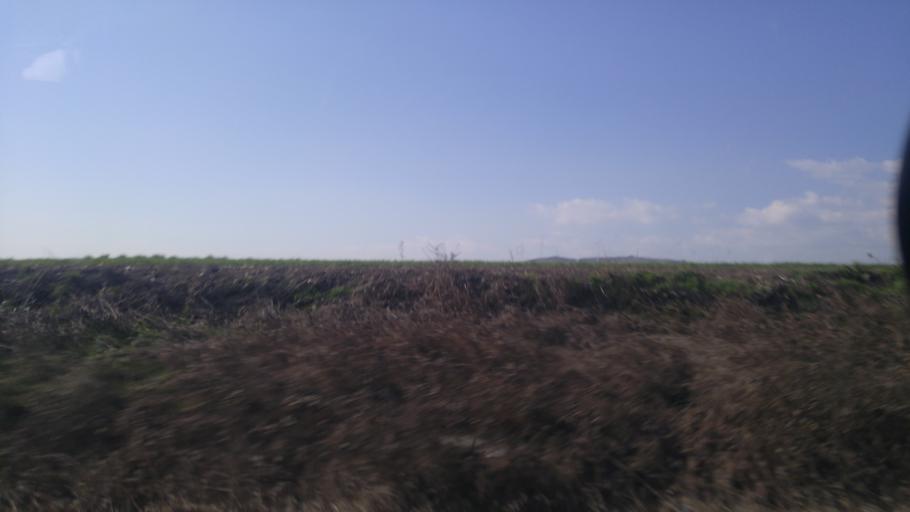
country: TR
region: Istanbul
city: Canta
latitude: 41.1002
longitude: 28.1106
